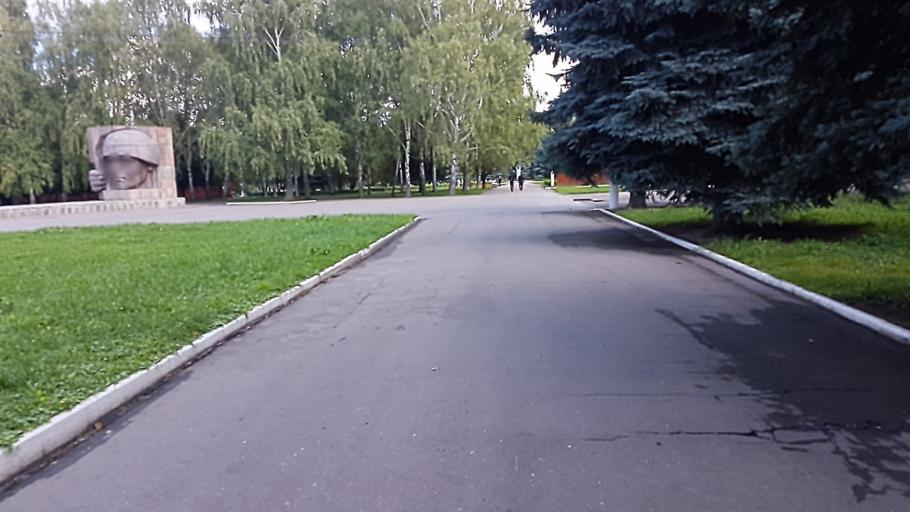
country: RU
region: Moskovskaya
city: Kolomna
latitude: 55.0943
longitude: 38.7700
